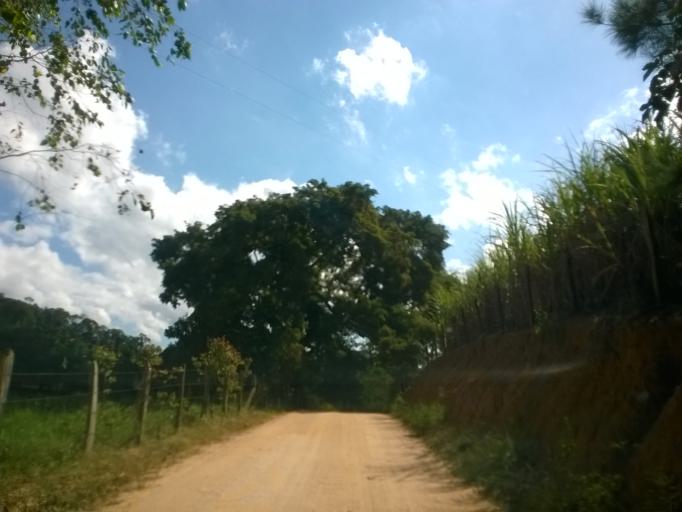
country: BR
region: Minas Gerais
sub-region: Visconde Do Rio Branco
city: Visconde do Rio Branco
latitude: -21.0505
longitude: -42.9001
